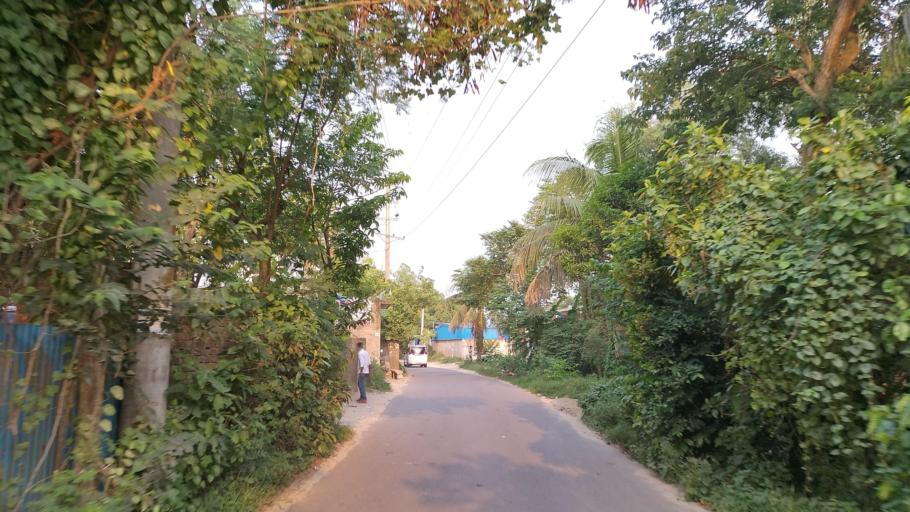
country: BD
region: Dhaka
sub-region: Dhaka
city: Dhaka
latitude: 23.6542
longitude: 90.3436
